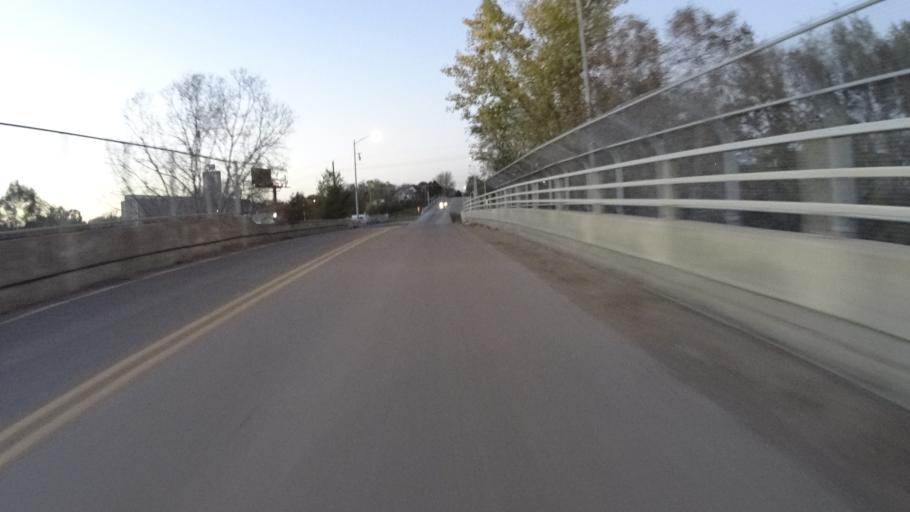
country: US
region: Nebraska
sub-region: Douglas County
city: Omaha
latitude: 41.2250
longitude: -95.9594
